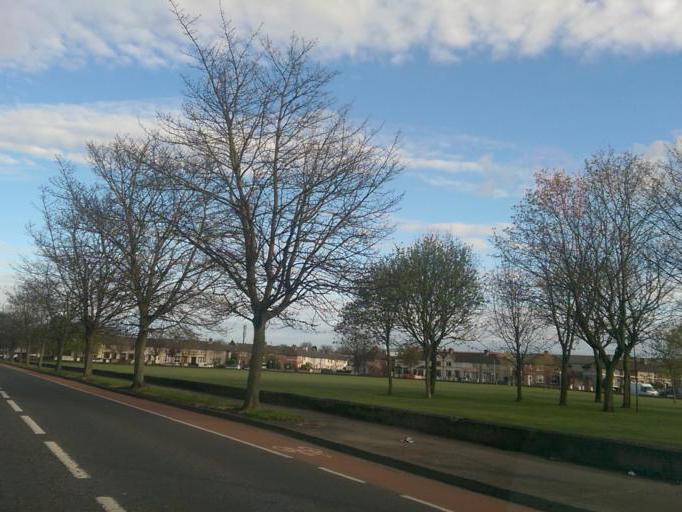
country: IE
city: Greenhills
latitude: 53.3353
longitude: -6.3028
